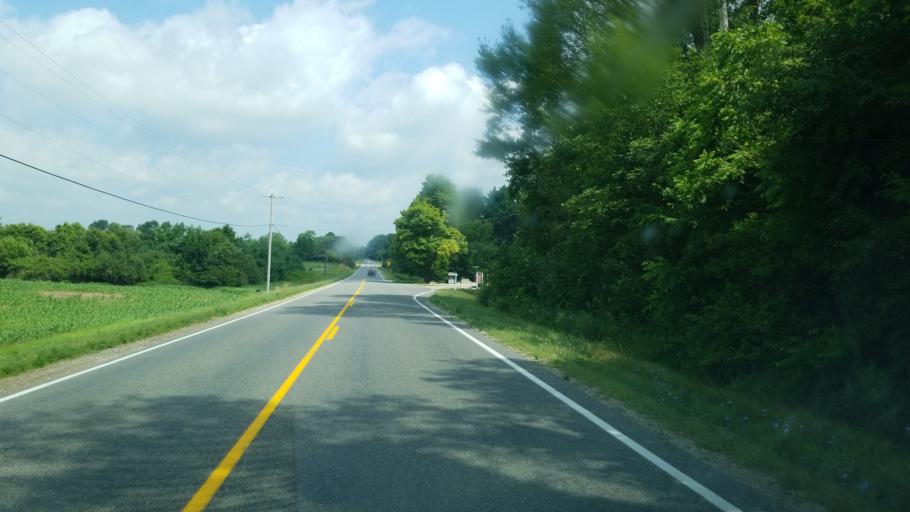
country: US
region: Michigan
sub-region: Kent County
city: Kent City
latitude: 43.2152
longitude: -85.7115
